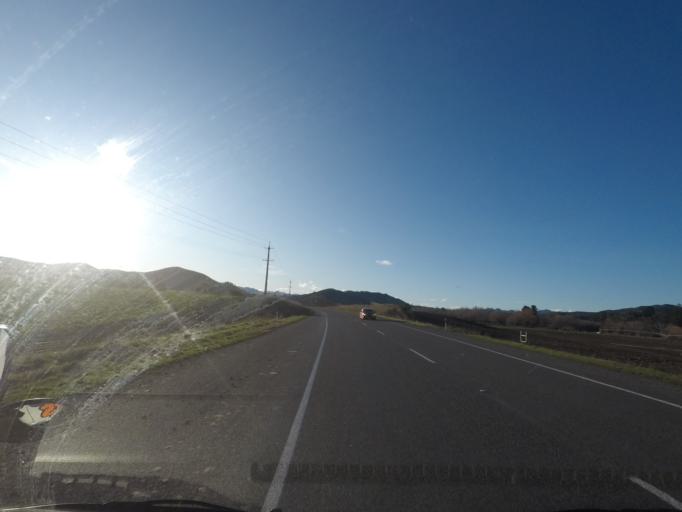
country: NZ
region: Canterbury
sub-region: Kaikoura District
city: Kaikoura
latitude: -42.6974
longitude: 173.3017
